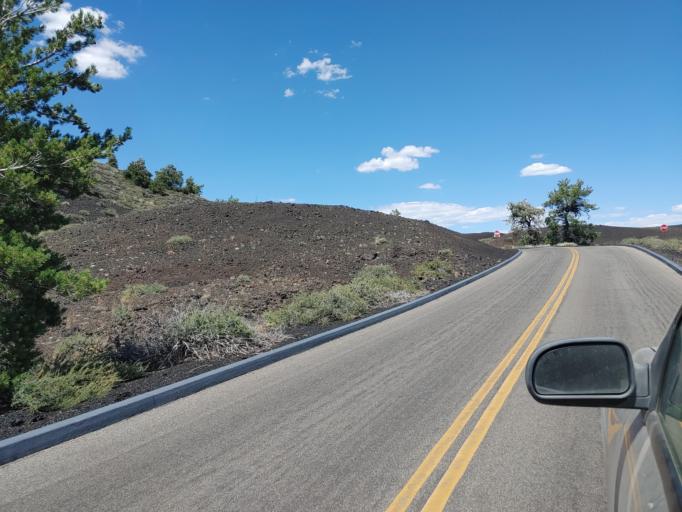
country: US
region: Idaho
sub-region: Butte County
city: Arco
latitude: 43.4427
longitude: -113.5570
